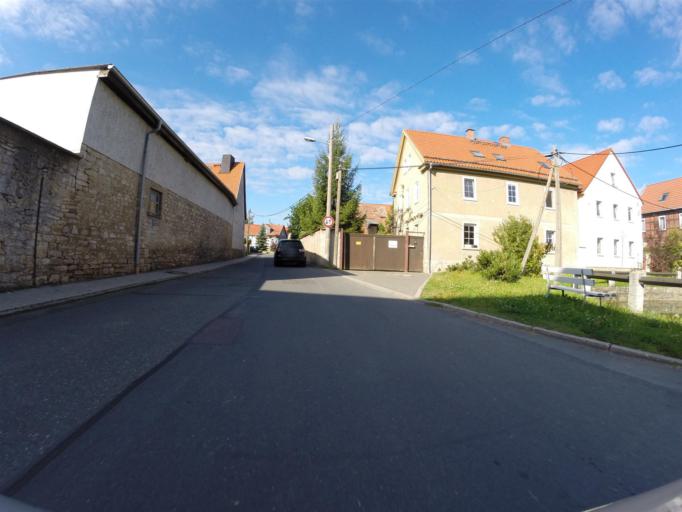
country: DE
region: Thuringia
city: Vollersroda
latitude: 50.9404
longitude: 11.3122
